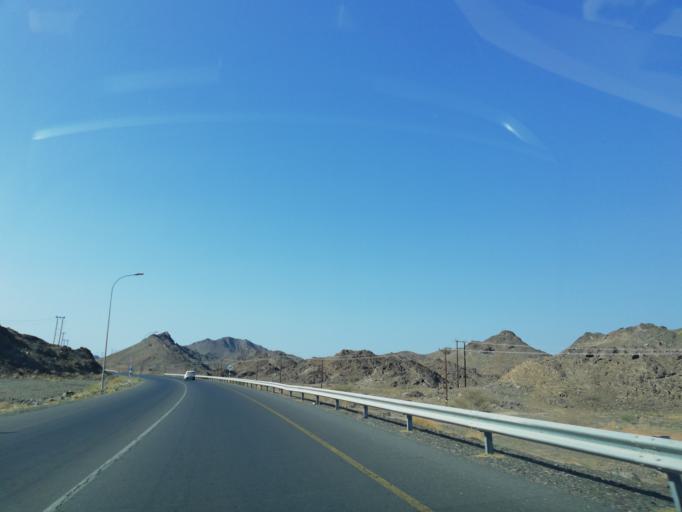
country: OM
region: Ash Sharqiyah
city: Ibra'
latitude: 22.8184
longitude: 58.1669
